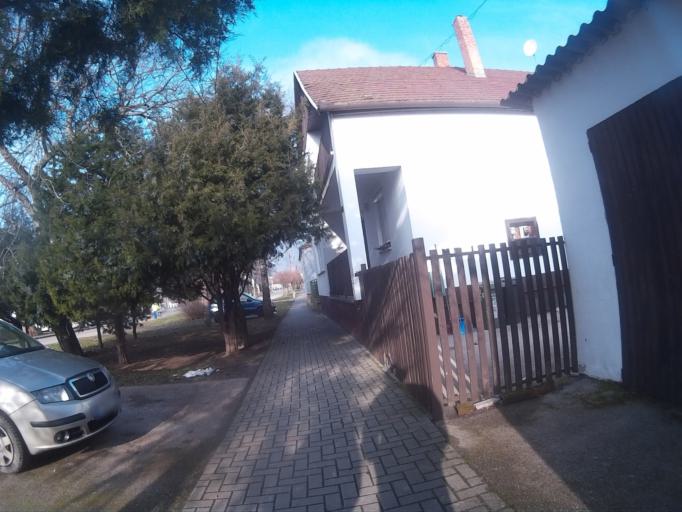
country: HU
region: Komarom-Esztergom
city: Tarjan
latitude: 47.6461
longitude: 18.5125
